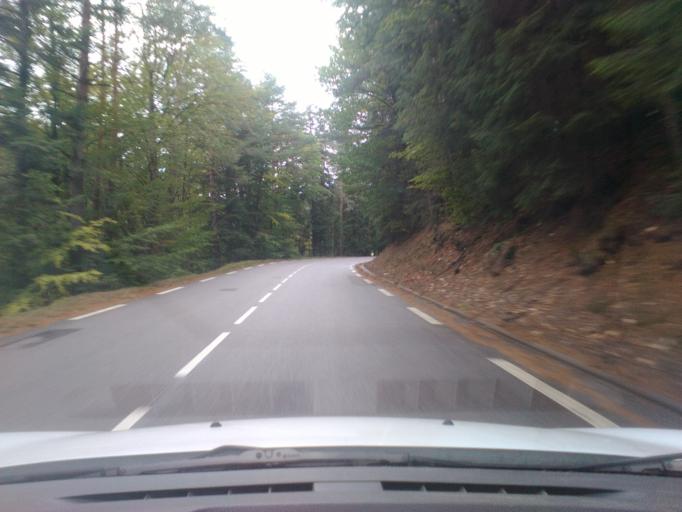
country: FR
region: Lorraine
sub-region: Departement des Vosges
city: Taintrux
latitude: 48.2720
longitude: 6.8781
